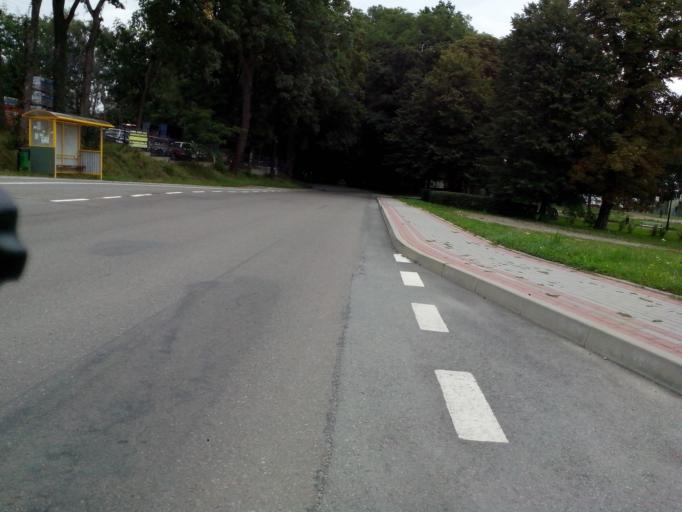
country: PL
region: Subcarpathian Voivodeship
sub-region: Powiat brzozowski
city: Jasienica Rosielna
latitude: 49.7554
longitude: 21.9485
